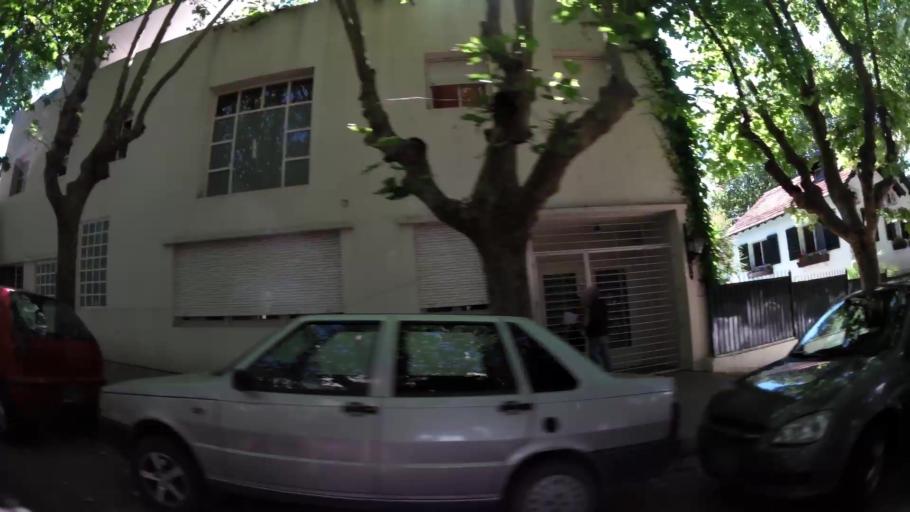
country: AR
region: Buenos Aires
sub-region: Partido de Vicente Lopez
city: Olivos
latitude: -34.5260
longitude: -58.4754
